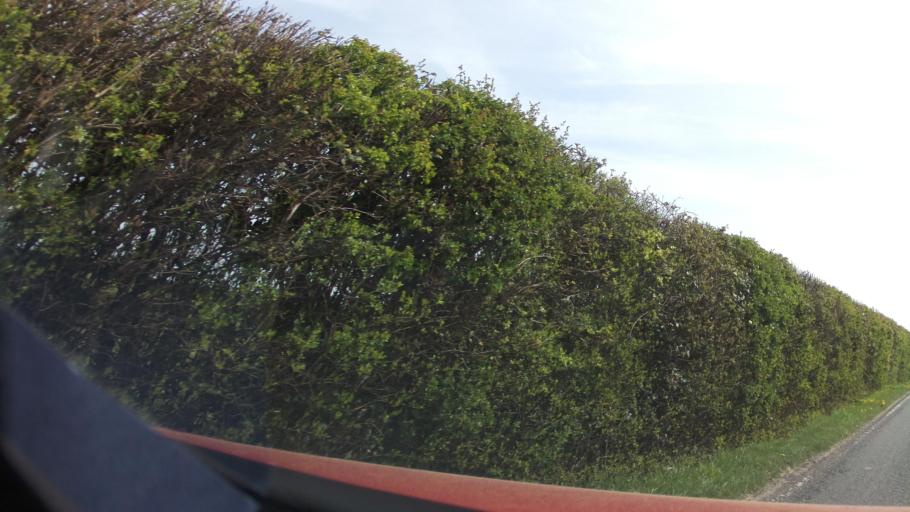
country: GB
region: England
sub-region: Somerset
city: Street
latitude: 51.1176
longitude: -2.7860
